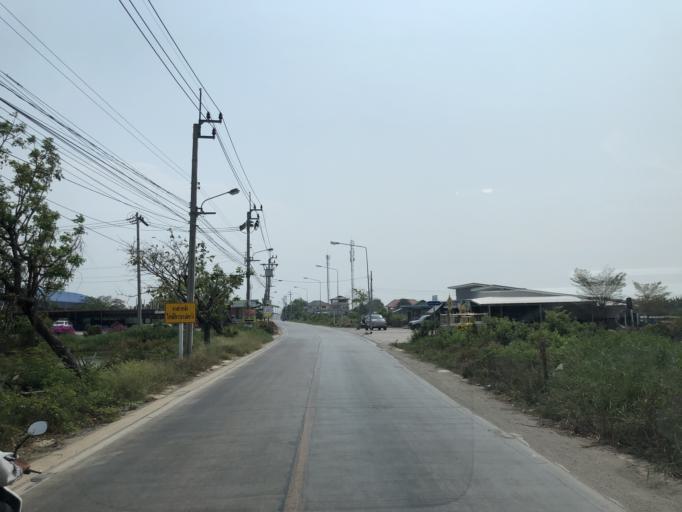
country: TH
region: Samut Prakan
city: Bang Bo
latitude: 13.5328
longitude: 100.8725
